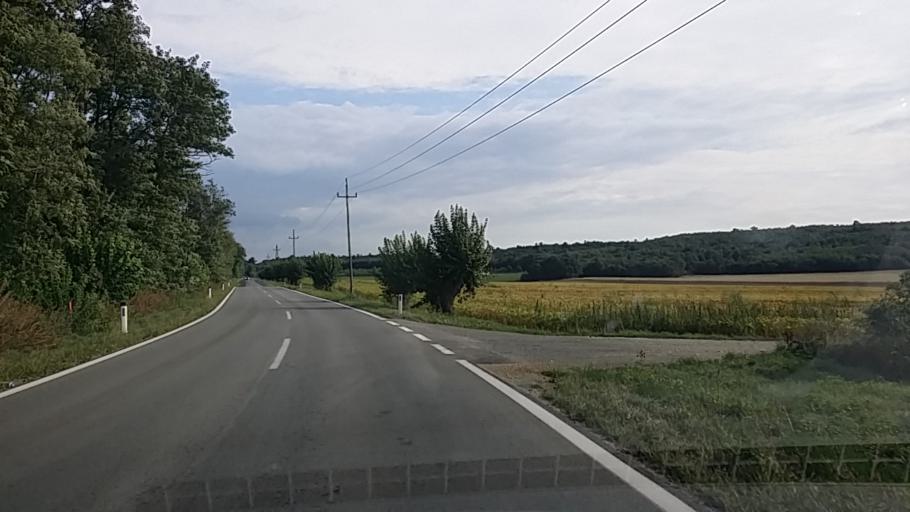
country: AT
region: Burgenland
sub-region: Eisenstadt-Umgebung
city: Sankt Margarethen im Burgenland
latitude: 47.7742
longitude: 16.6165
